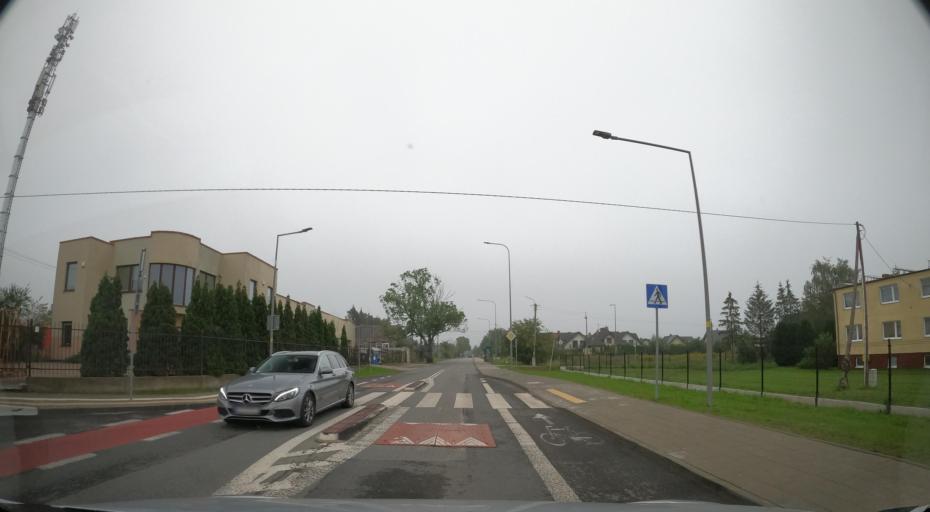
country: PL
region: Pomeranian Voivodeship
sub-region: Powiat kartuski
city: Chwaszczyno
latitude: 54.4209
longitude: 18.4529
